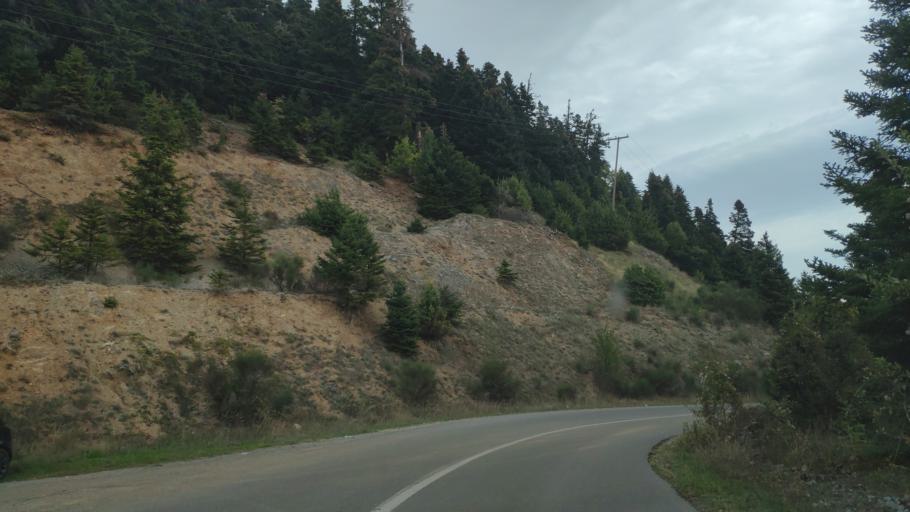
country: GR
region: Central Greece
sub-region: Nomos Fthiotidos
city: Stavros
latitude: 38.7223
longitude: 22.3300
